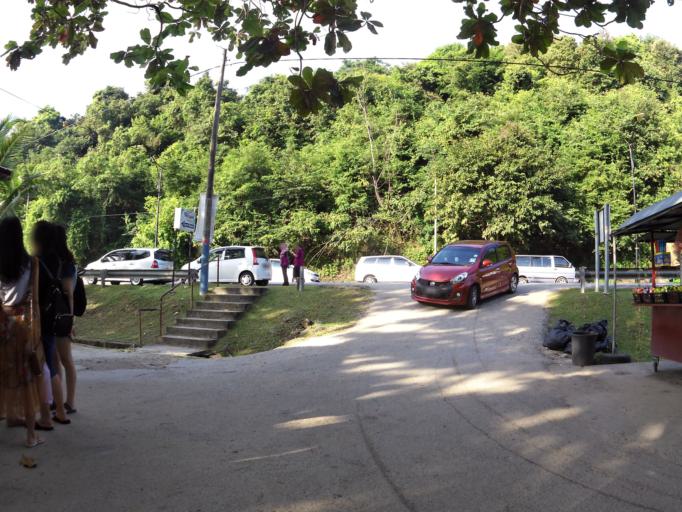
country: MY
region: Kedah
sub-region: Langkawi
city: Kuah
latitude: 6.2659
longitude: 99.7353
